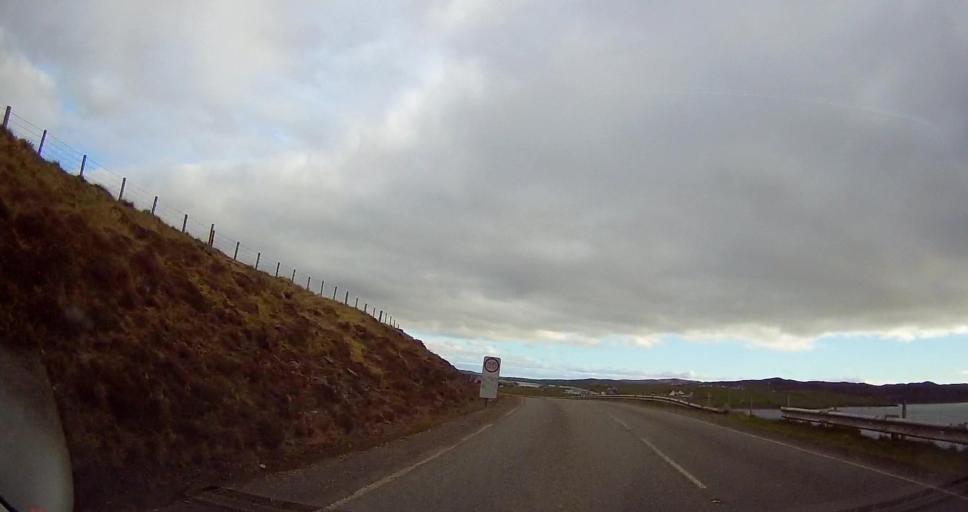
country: GB
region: Scotland
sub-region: Shetland Islands
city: Lerwick
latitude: 60.4049
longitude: -1.3477
